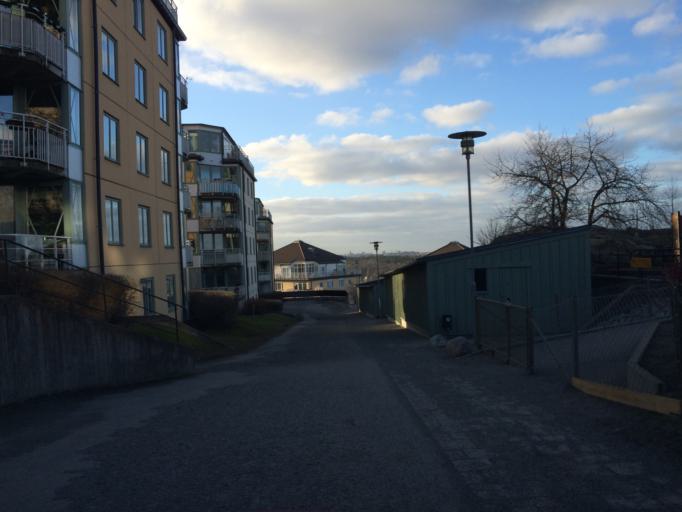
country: SE
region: Stockholm
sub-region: Nacka Kommun
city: Nacka
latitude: 59.3165
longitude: 18.1638
